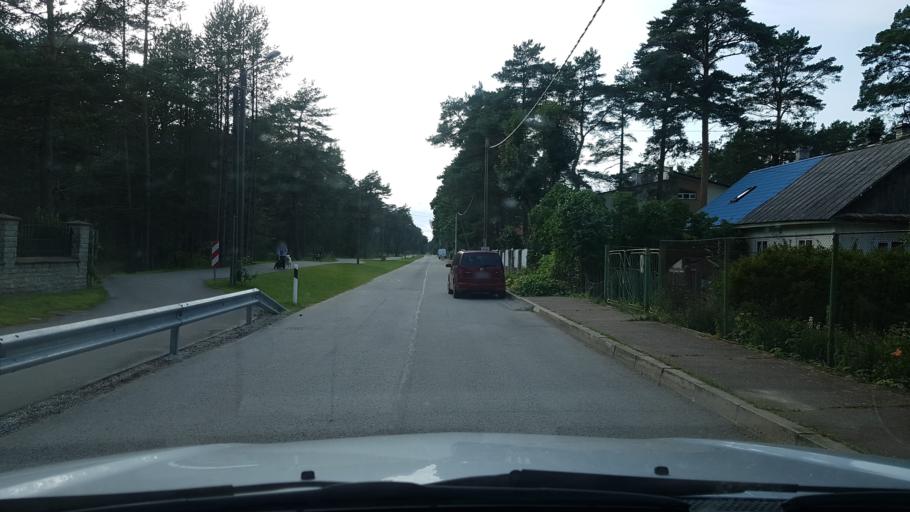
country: EE
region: Ida-Virumaa
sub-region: Narva-Joesuu linn
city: Narva-Joesuu
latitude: 59.4534
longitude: 28.0525
